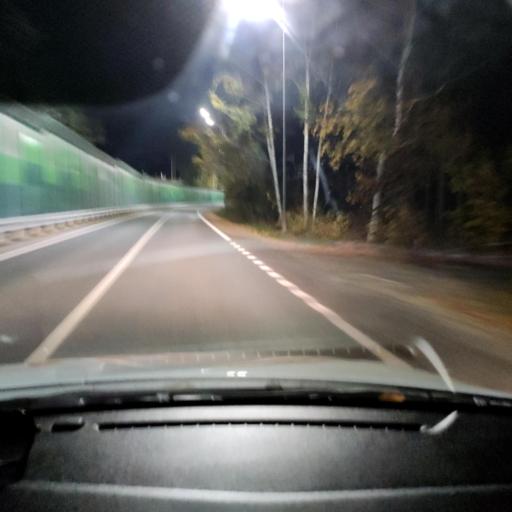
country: RU
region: Tatarstan
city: Verkhniy Uslon
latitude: 55.6277
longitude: 49.0141
